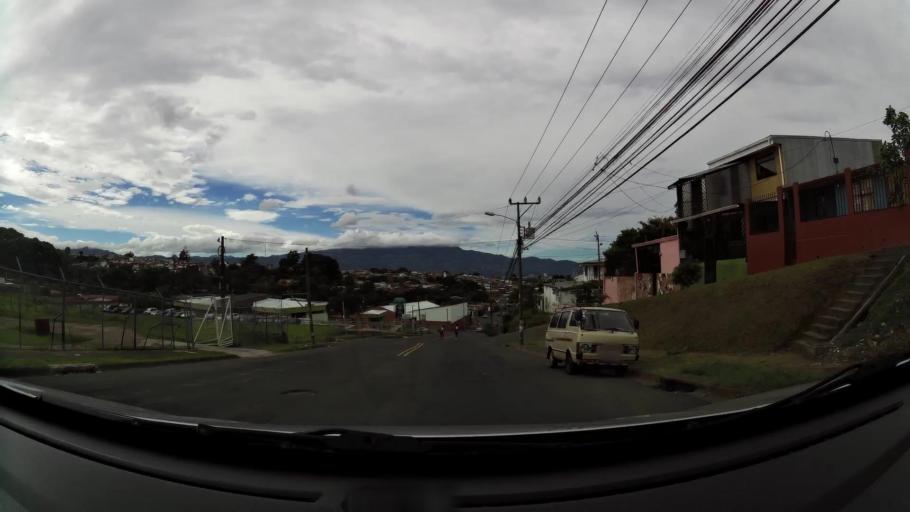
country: CR
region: San Jose
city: Purral
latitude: 9.9569
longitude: -84.0311
